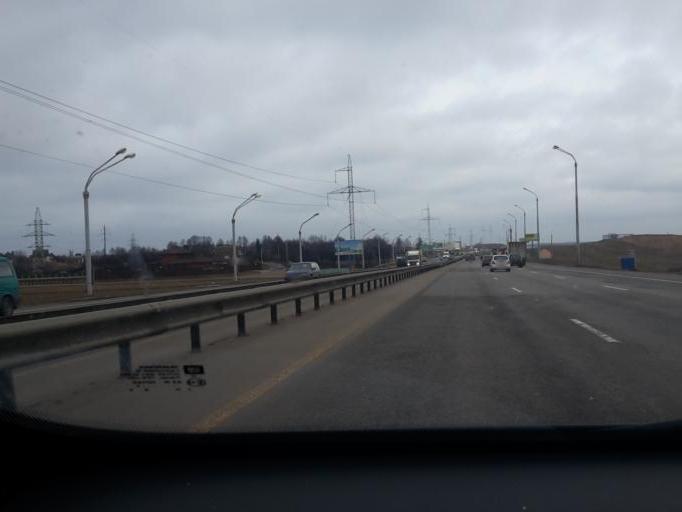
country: BY
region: Minsk
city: Zhdanovichy
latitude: 53.9229
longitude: 27.4159
